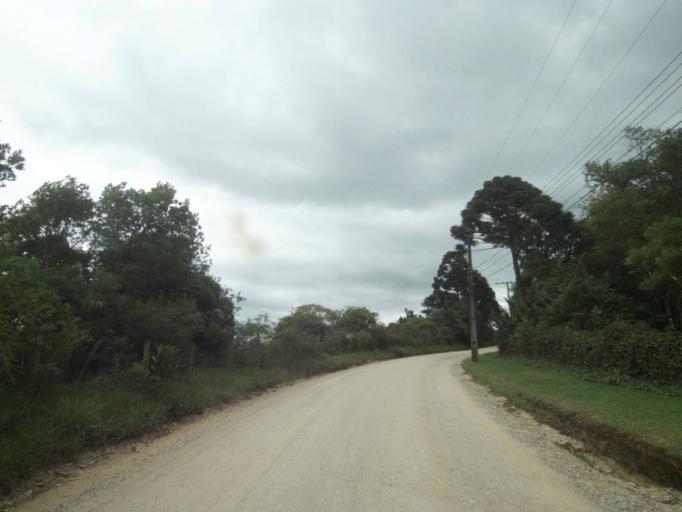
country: BR
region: Parana
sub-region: Campina Grande Do Sul
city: Campina Grande do Sul
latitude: -25.3234
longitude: -49.0834
